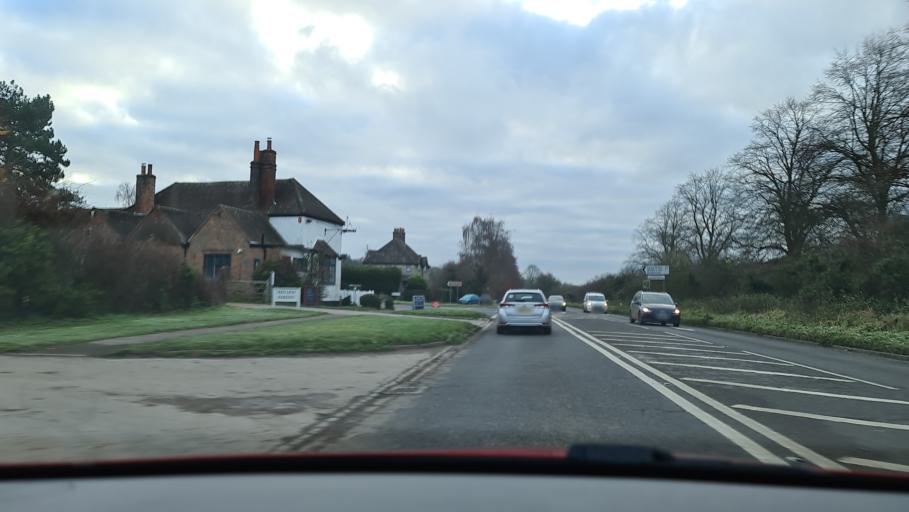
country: GB
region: England
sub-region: Buckinghamshire
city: Princes Risborough
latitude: 51.6661
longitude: -0.8110
